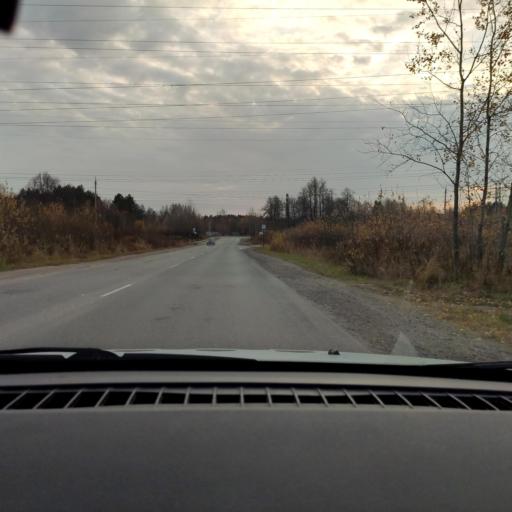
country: RU
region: Perm
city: Perm
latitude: 58.0965
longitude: 56.4050
